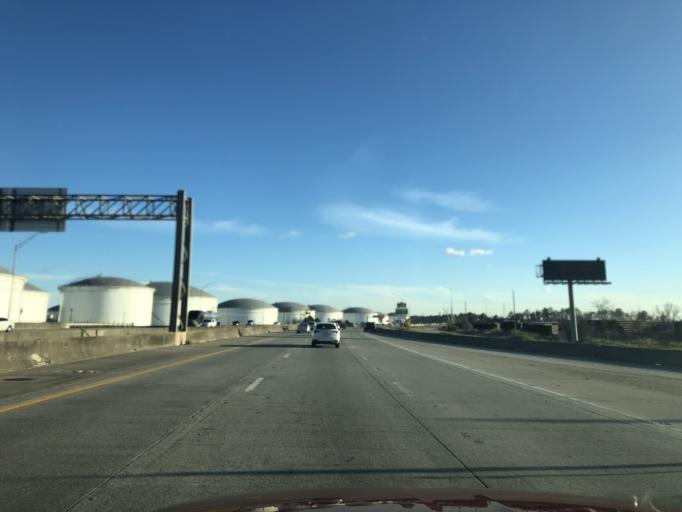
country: US
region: Texas
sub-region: Harris County
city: Cloverleaf
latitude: 29.7653
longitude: -95.1485
